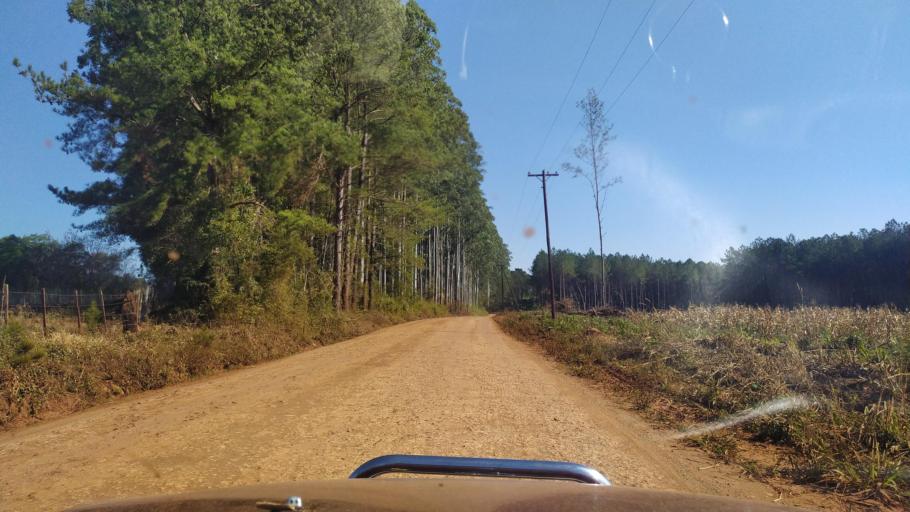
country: AR
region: Misiones
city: El Alcazar
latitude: -26.7150
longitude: -54.7054
